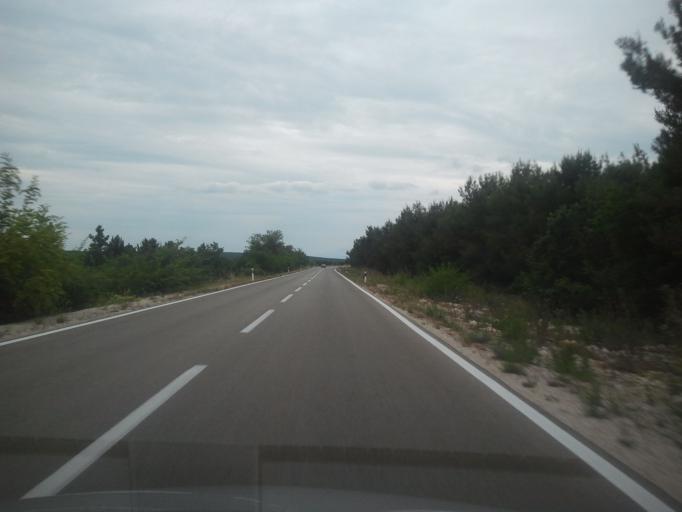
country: HR
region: Zadarska
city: Benkovac
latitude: 44.0667
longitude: 15.6067
